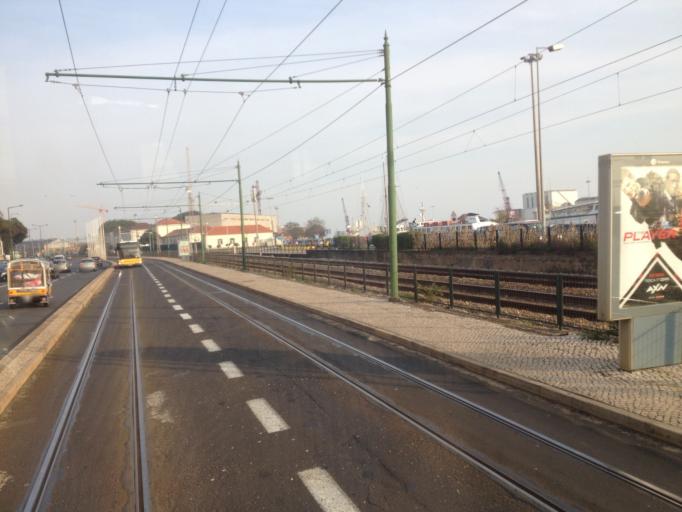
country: PT
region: Setubal
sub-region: Almada
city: Cacilhas
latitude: 38.7035
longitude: -9.1652
